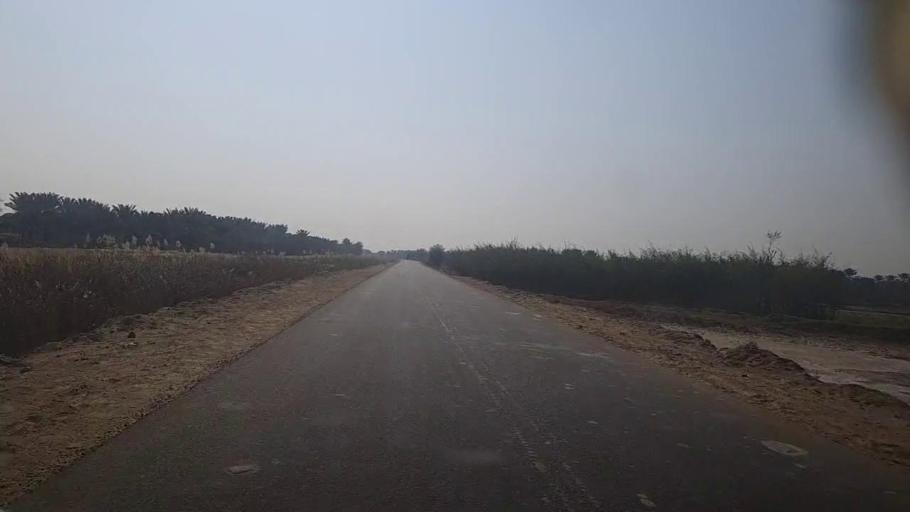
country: PK
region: Sindh
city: Khairpur
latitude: 27.4696
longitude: 68.8204
